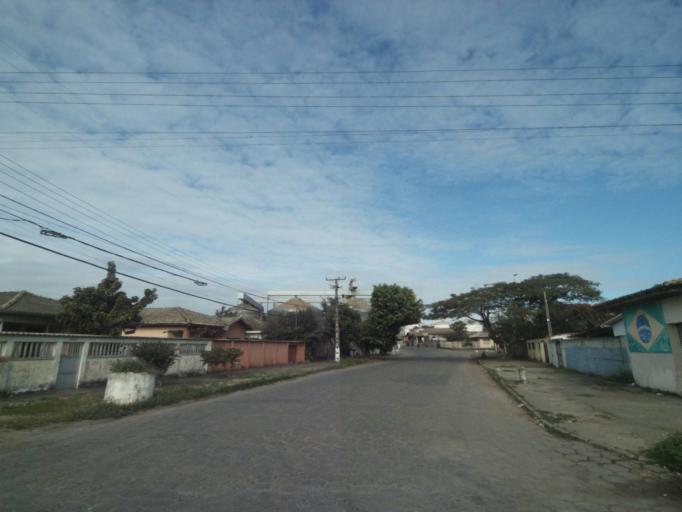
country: BR
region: Parana
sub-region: Paranagua
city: Paranagua
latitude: -25.5104
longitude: -48.5266
